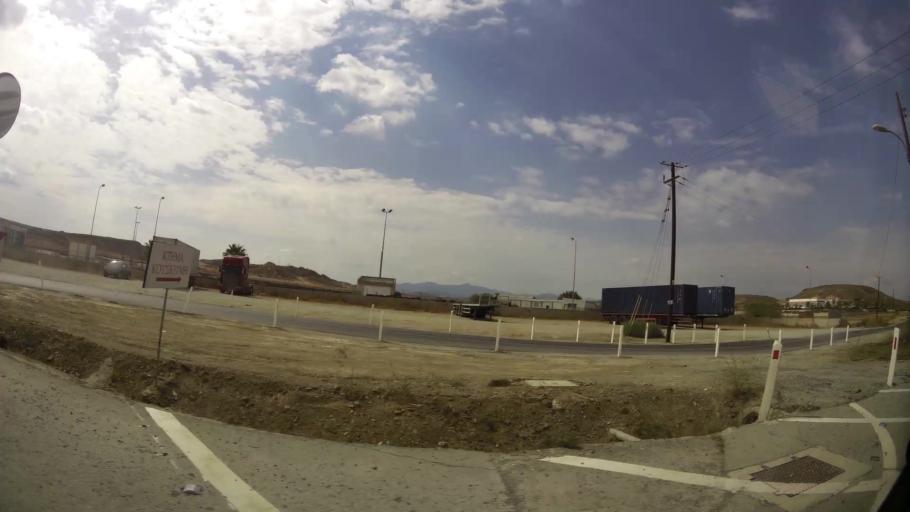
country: CY
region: Lefkosia
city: Tseri
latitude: 35.0541
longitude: 33.3753
